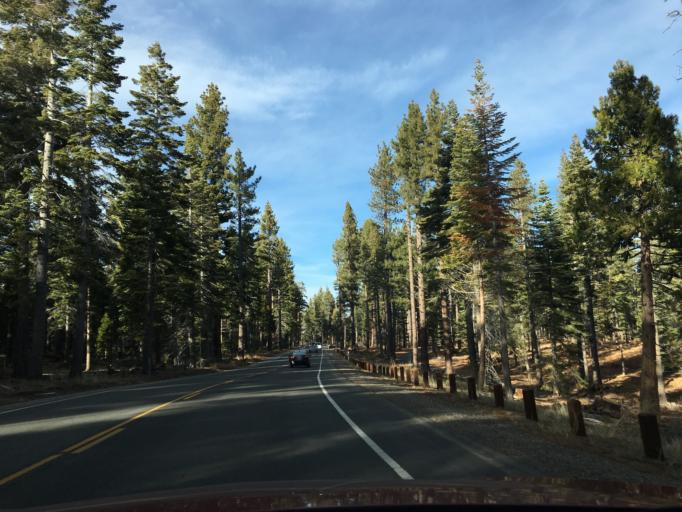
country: US
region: California
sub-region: El Dorado County
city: South Lake Tahoe
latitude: 38.9268
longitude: -120.0303
